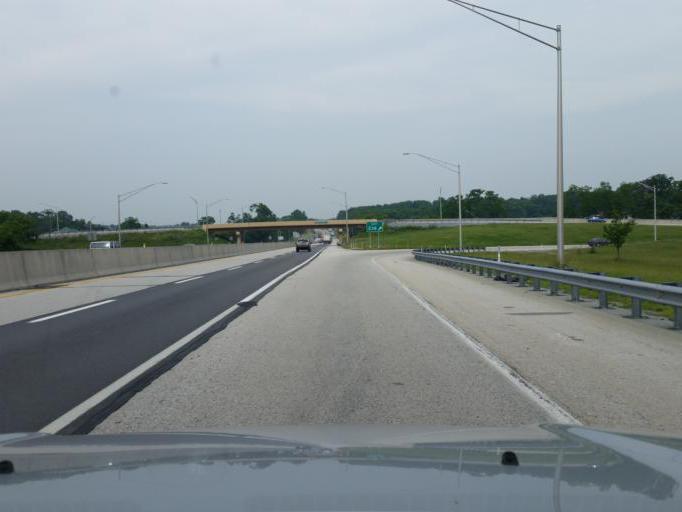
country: US
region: Pennsylvania
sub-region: Cumberland County
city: Shiremanstown
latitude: 40.1958
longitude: -76.9767
